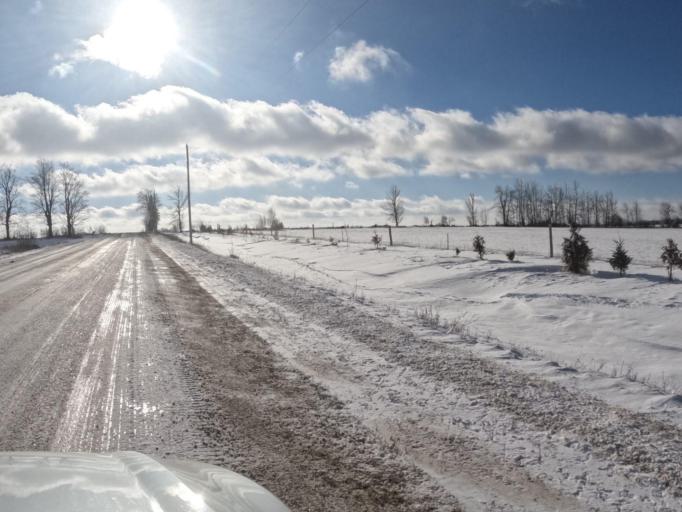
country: CA
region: Ontario
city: Shelburne
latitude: 43.9893
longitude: -80.4070
